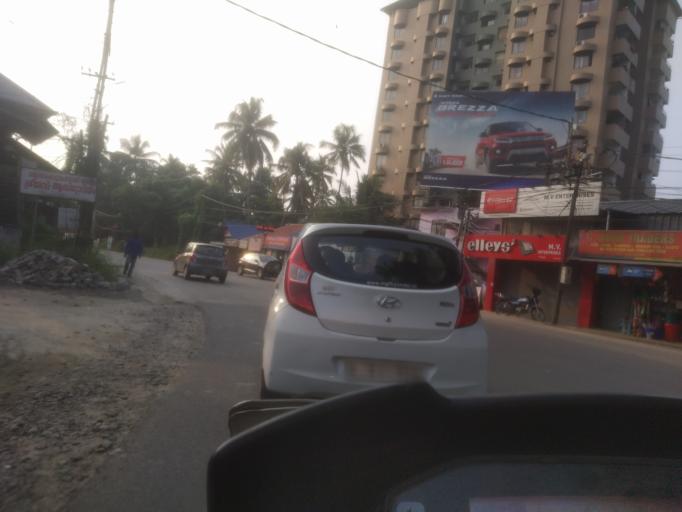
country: IN
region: Kerala
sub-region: Ernakulam
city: Cochin
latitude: 9.9389
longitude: 76.3266
